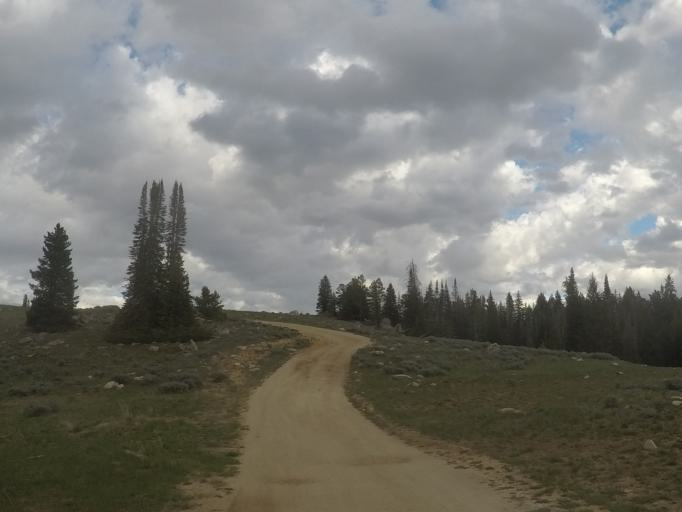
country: US
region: Wyoming
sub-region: Sheridan County
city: Sheridan
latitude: 44.5035
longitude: -107.4356
